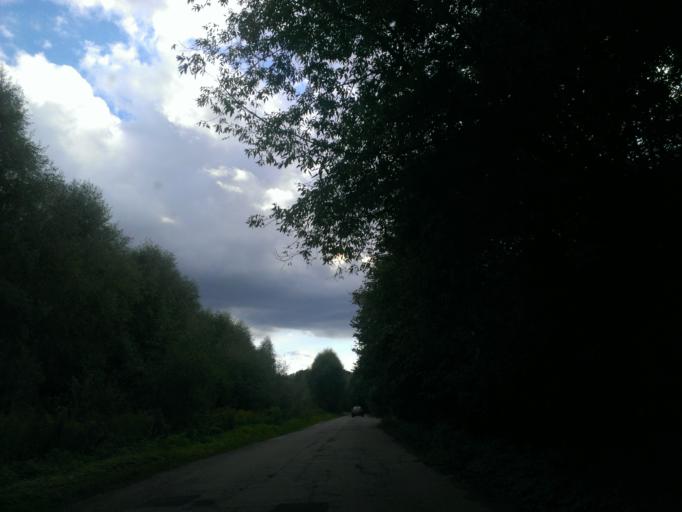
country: LV
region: Sigulda
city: Sigulda
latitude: 57.1570
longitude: 24.8371
